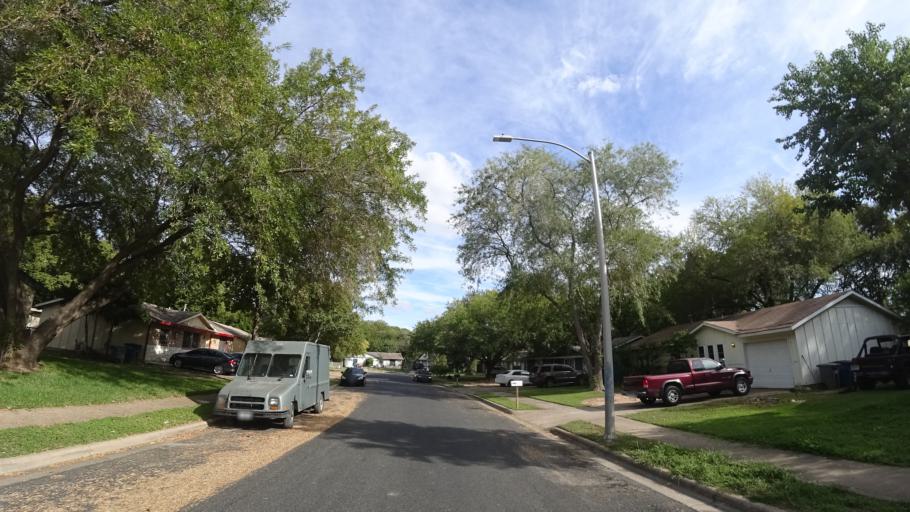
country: US
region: Texas
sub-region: Travis County
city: Austin
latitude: 30.1990
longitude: -97.7542
